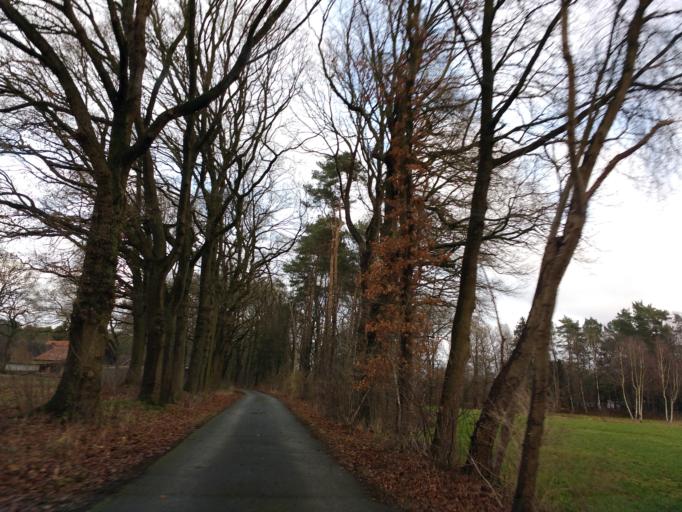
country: DE
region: North Rhine-Westphalia
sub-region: Regierungsbezirk Detmold
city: Hovelhof
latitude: 51.8155
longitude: 8.7062
